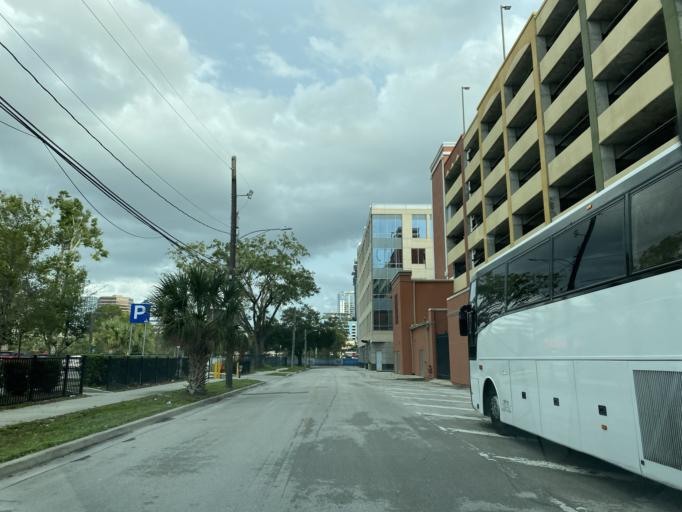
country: US
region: Florida
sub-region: Orange County
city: Orlando
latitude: 28.5411
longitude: -81.3862
